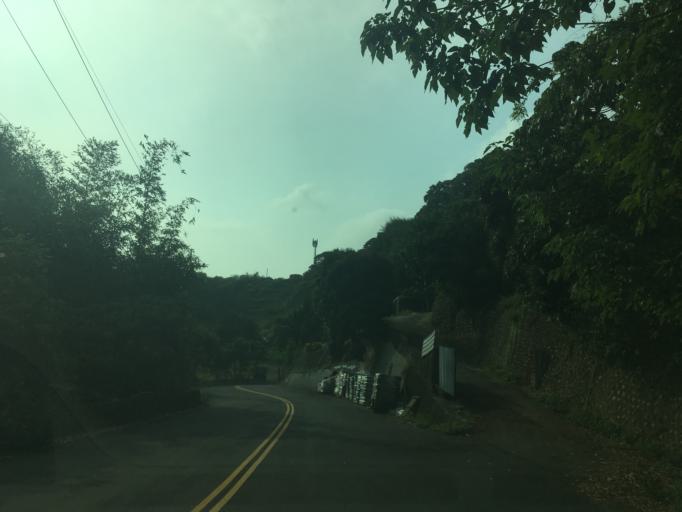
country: TW
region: Taiwan
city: Fengyuan
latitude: 24.2262
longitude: 120.7563
